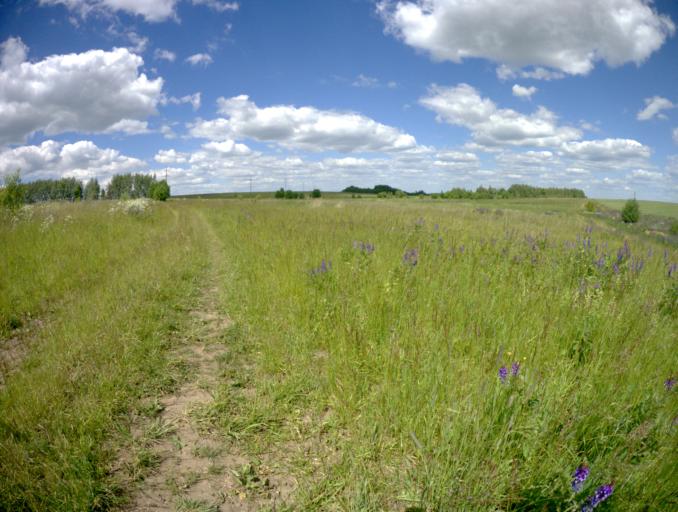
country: RU
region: Vladimir
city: Bogolyubovo
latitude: 56.2688
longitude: 40.4164
